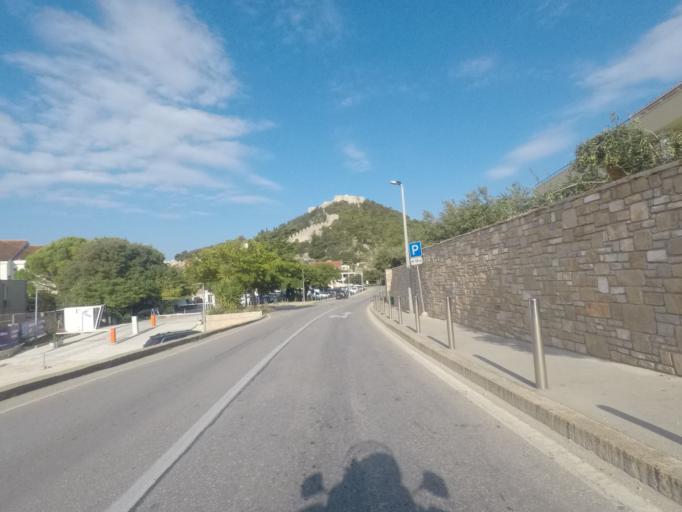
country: HR
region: Splitsko-Dalmatinska
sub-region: Grad Hvar
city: Hvar
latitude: 43.1729
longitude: 16.4461
